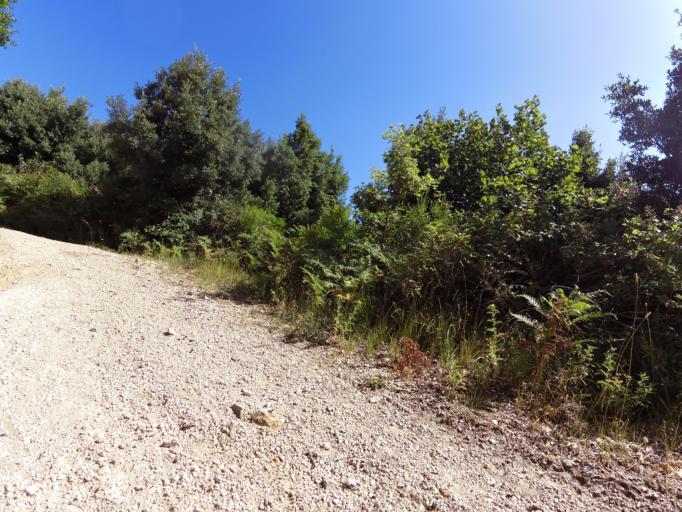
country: IT
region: Calabria
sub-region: Provincia di Reggio Calabria
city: Bivongi
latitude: 38.5037
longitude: 16.4404
